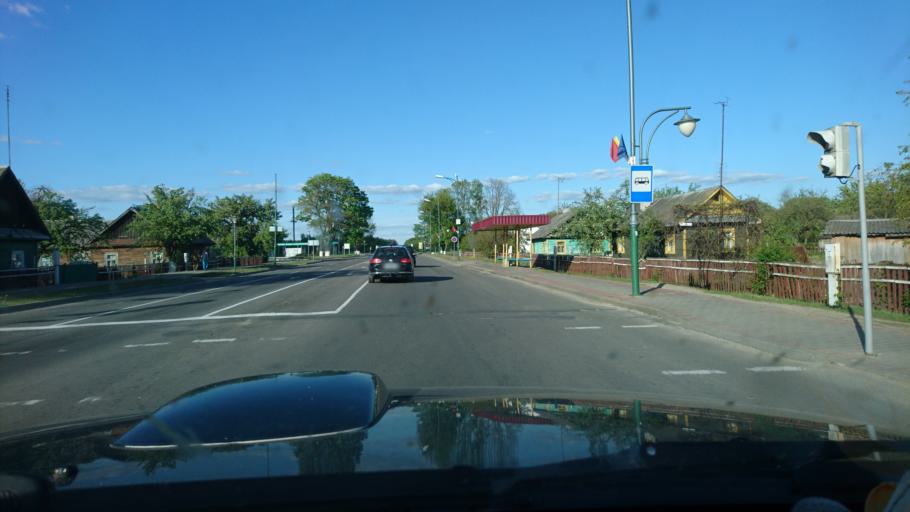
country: BY
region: Brest
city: Byaroza
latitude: 52.5392
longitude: 24.9945
